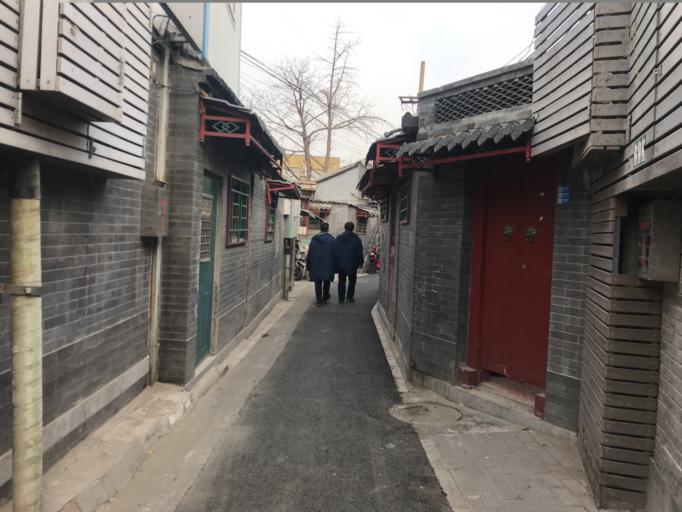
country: CN
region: Beijing
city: Beijing
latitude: 39.8902
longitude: 116.3857
